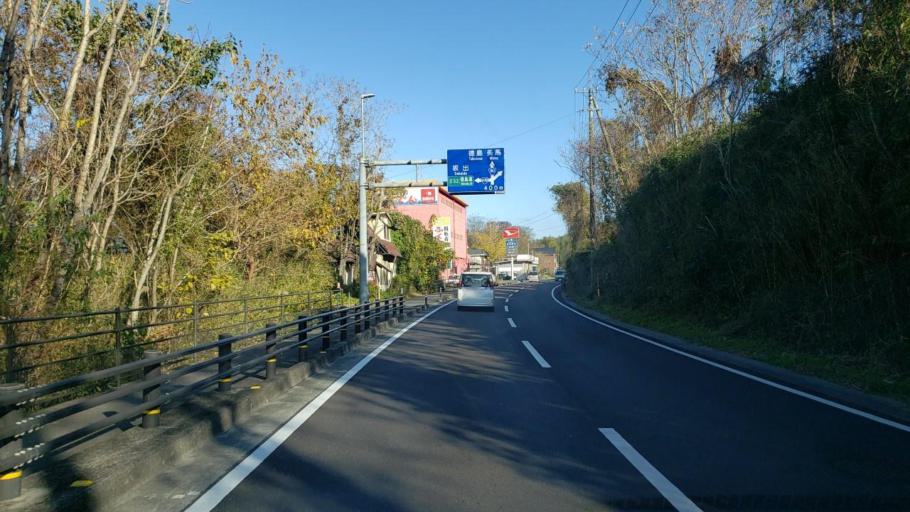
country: JP
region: Tokushima
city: Wakimachi
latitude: 34.0426
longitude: 134.0466
